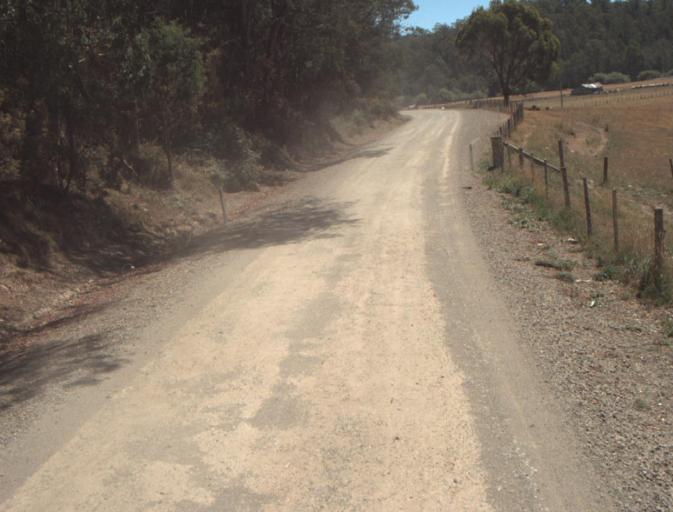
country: AU
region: Tasmania
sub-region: Dorset
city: Scottsdale
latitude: -41.2876
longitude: 147.3889
